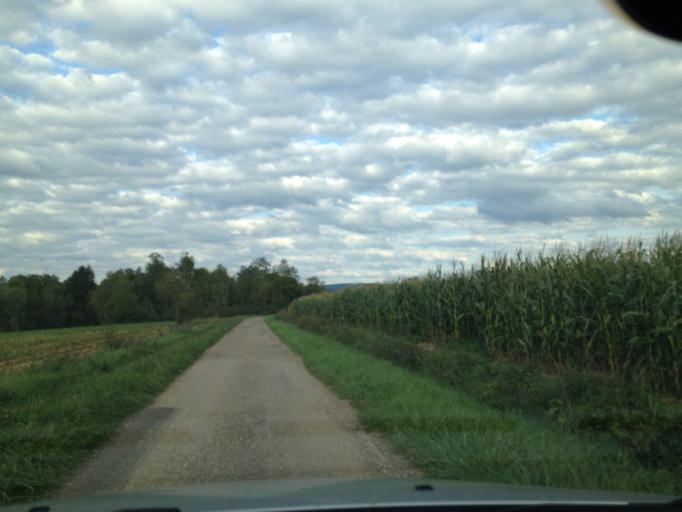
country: FR
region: Lorraine
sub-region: Departement des Vosges
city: Bains-les-Bains
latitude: 47.9717
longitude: 6.1381
